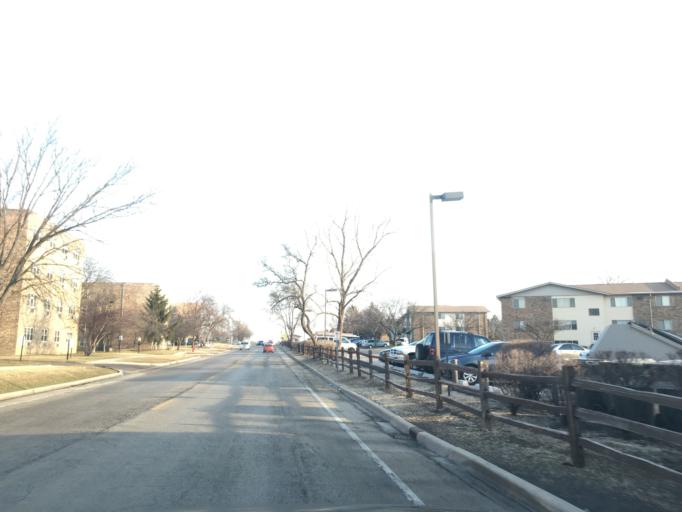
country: US
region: Illinois
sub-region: Cook County
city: Schaumburg
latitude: 42.0383
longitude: -88.1020
